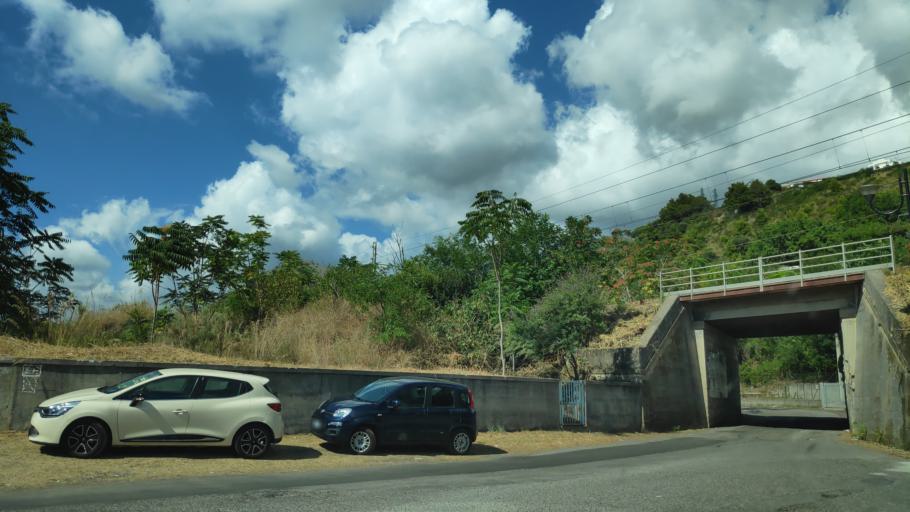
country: IT
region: Calabria
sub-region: Provincia di Cosenza
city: Praia a Mare
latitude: 39.8735
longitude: 15.7873
